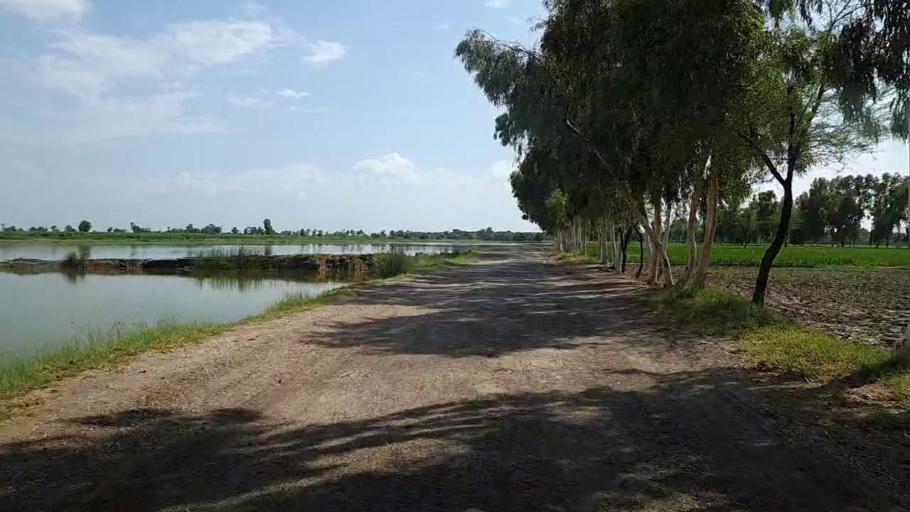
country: PK
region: Sindh
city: Bhiria
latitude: 26.9151
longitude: 68.2292
